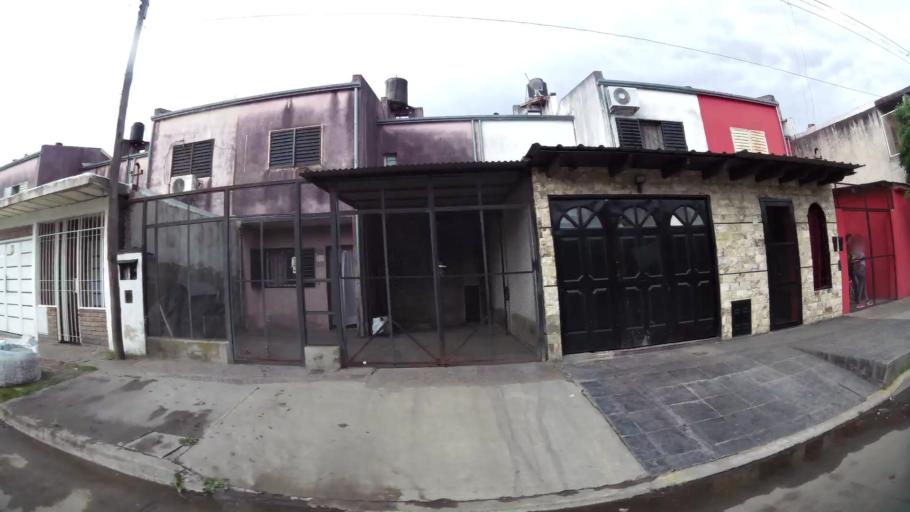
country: AR
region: Santa Fe
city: Gobernador Galvez
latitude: -33.0011
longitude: -60.6879
